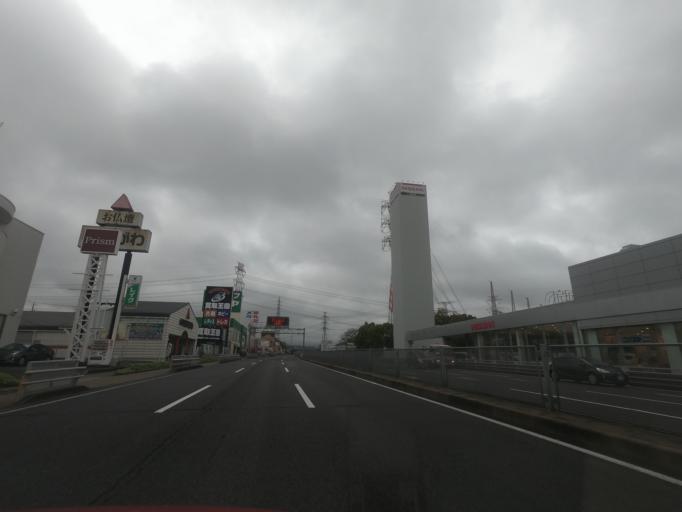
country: JP
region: Aichi
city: Kasugai
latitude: 35.2653
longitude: 136.9919
